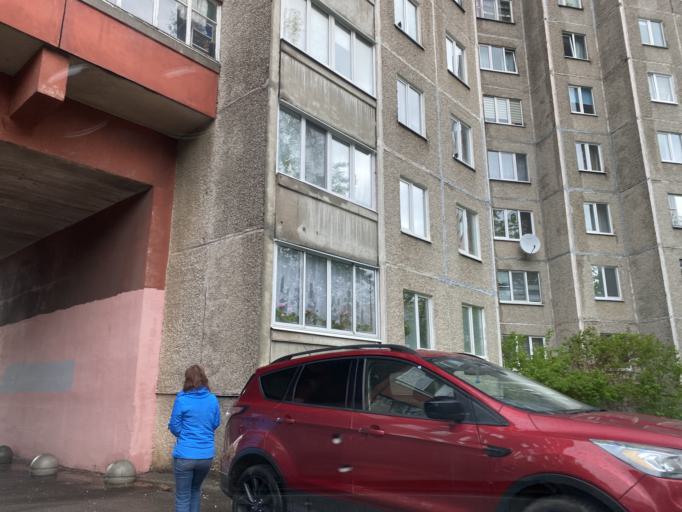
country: BY
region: Minsk
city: Bal'shavik
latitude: 53.9584
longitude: 27.6126
